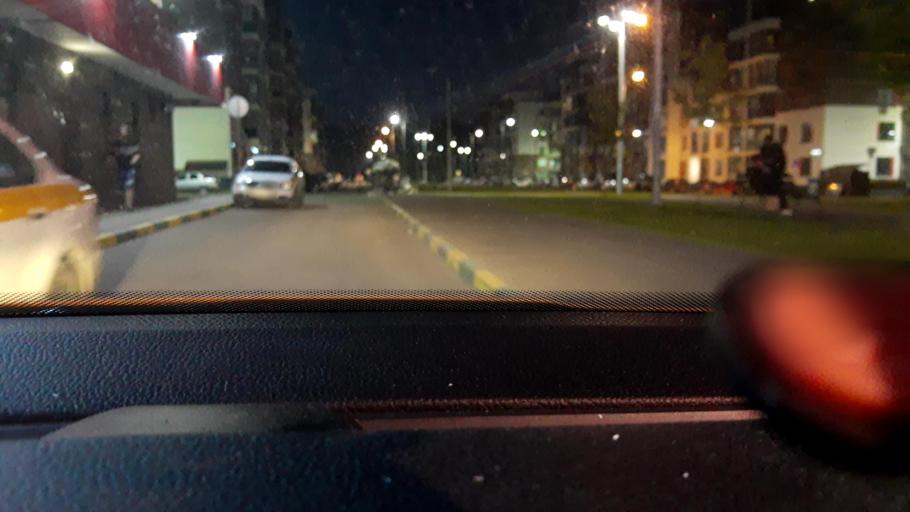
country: RU
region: Moskovskaya
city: Pirogovskiy
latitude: 55.9574
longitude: 37.6839
